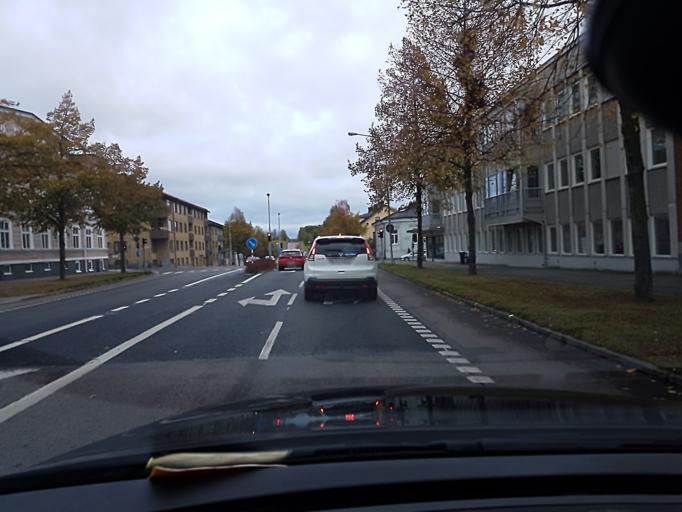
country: SE
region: Kronoberg
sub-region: Vaxjo Kommun
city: Vaexjoe
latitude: 56.8814
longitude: 14.8082
